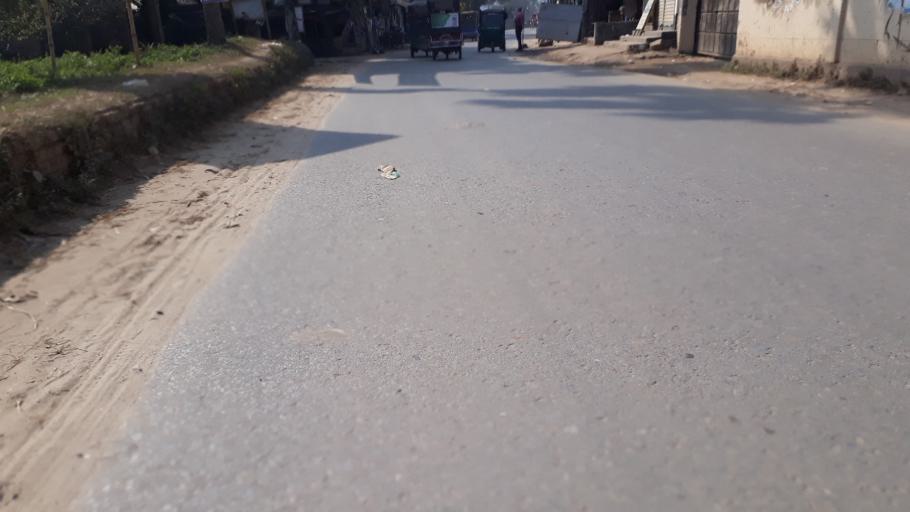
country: BD
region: Dhaka
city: Tungi
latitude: 23.9086
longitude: 90.2939
